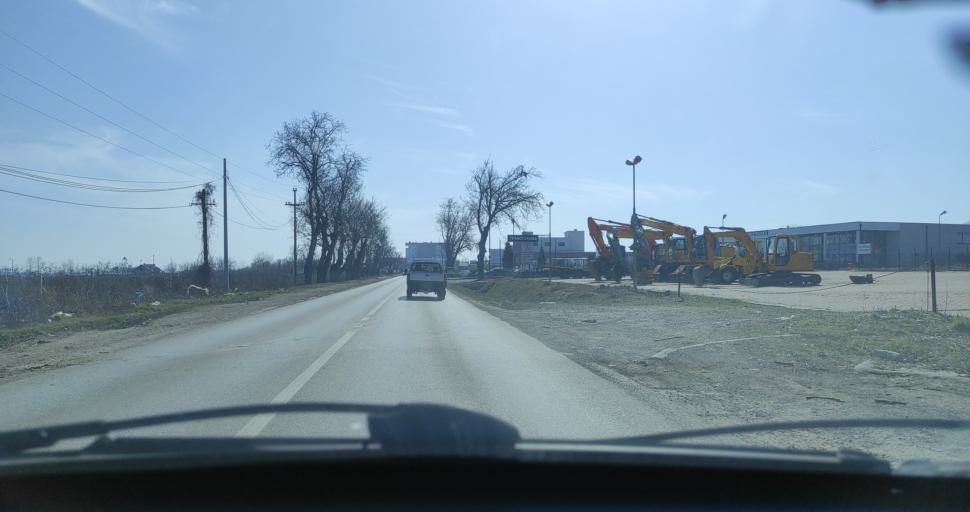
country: XK
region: Pec
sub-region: Komuna e Pejes
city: Peje
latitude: 42.6315
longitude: 20.3038
